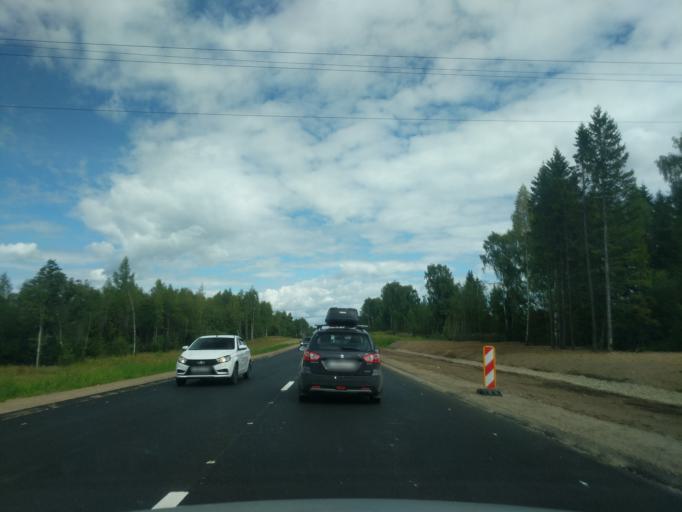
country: RU
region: Kostroma
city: Kosmynino
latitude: 57.7207
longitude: 40.7813
